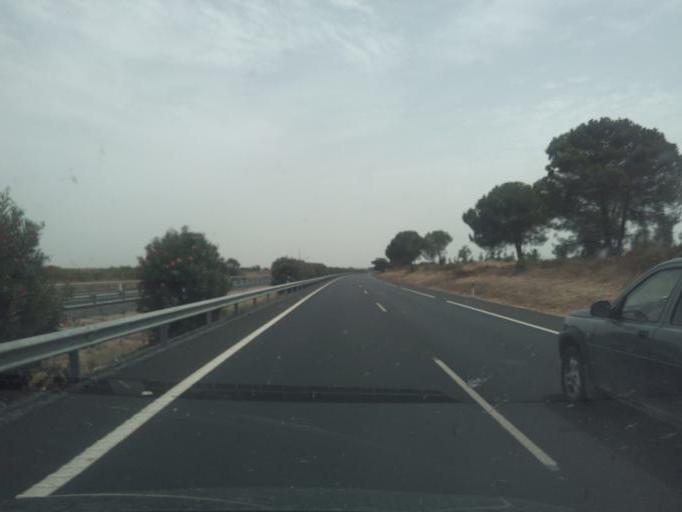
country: ES
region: Andalusia
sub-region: Provincia de Huelva
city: Bollullos par del Condado
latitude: 37.3566
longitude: -6.4984
